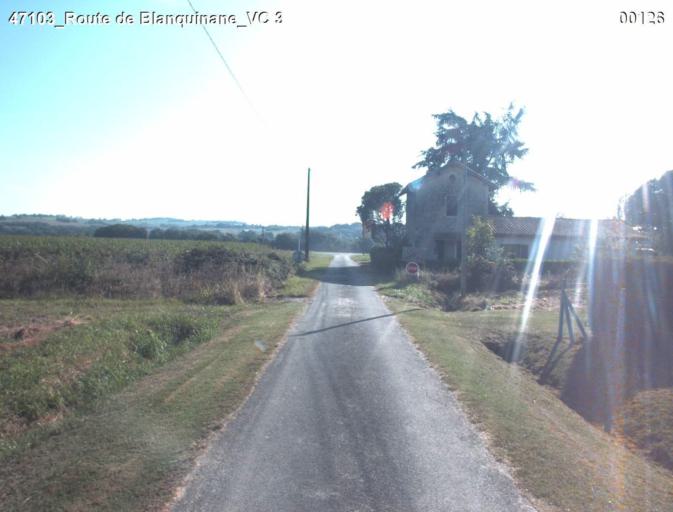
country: FR
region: Aquitaine
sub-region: Departement du Lot-et-Garonne
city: Nerac
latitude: 44.0856
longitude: 0.3618
